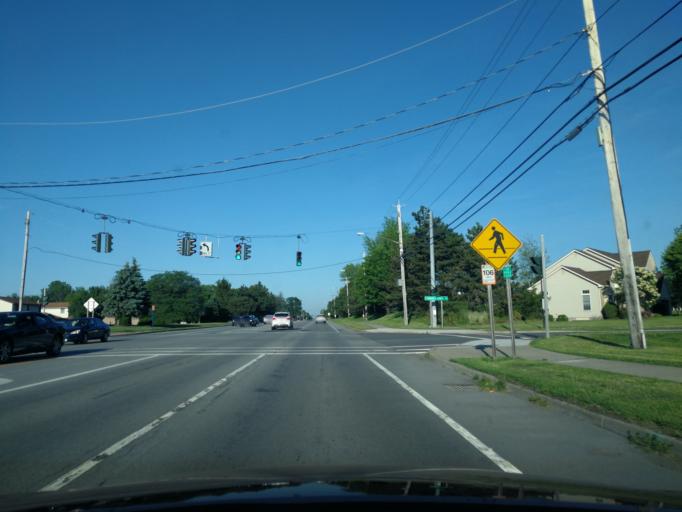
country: US
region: New York
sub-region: Monroe County
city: Greece
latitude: 43.2530
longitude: -77.7071
